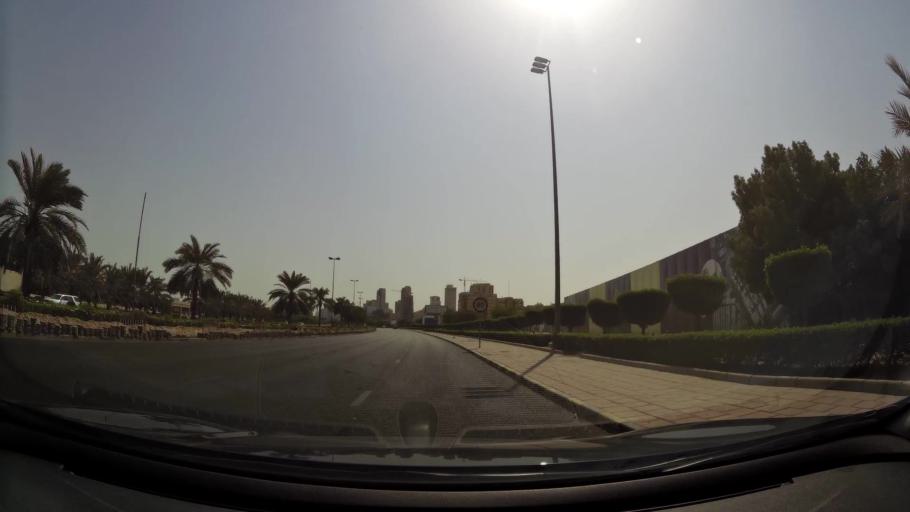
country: KW
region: Al Asimah
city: Ad Dasmah
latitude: 29.3638
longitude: 48.0224
